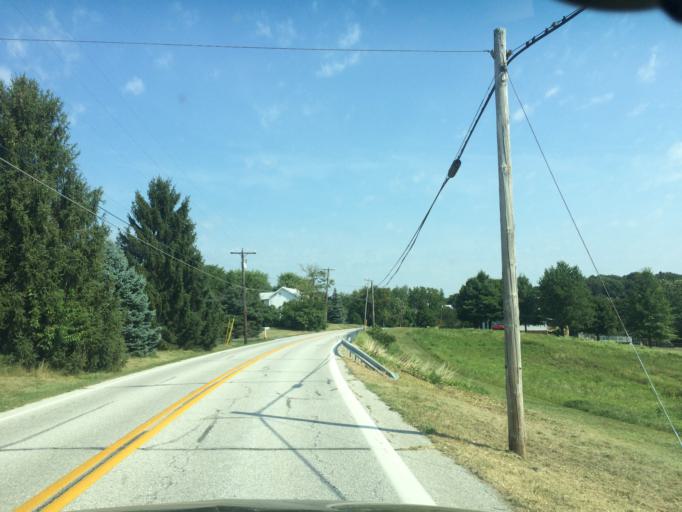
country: US
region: Maryland
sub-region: Carroll County
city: New Windsor
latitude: 39.5790
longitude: -77.1258
